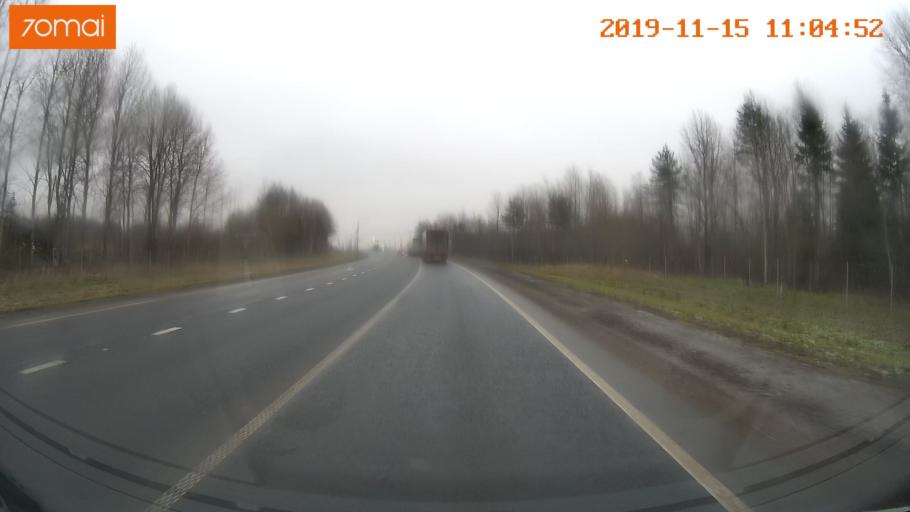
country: RU
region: Vologda
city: Chebsara
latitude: 59.1185
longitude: 38.9929
